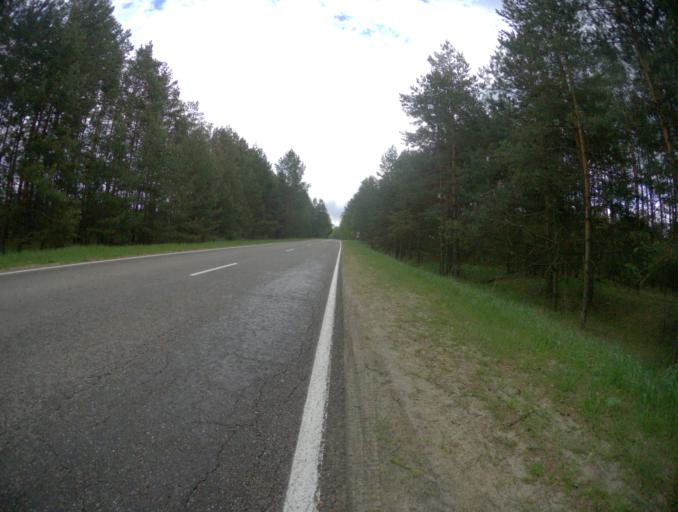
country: RU
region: Vladimir
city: Gusevskiy
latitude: 55.5753
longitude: 40.5069
